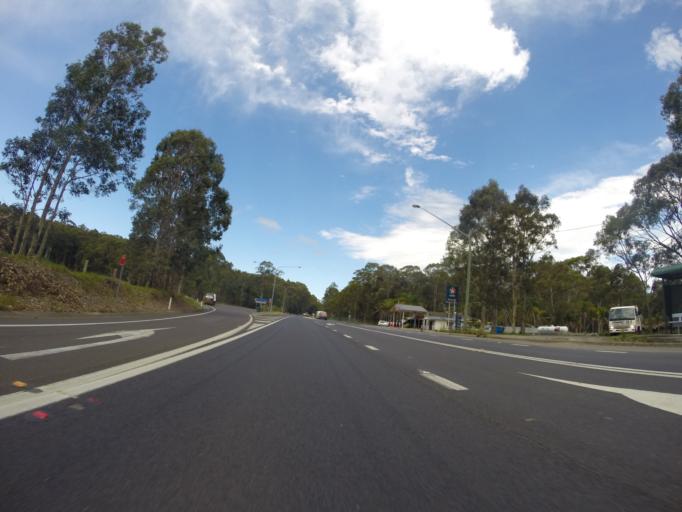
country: AU
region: New South Wales
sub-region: Shoalhaven Shire
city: Falls Creek
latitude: -35.0852
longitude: 150.5313
